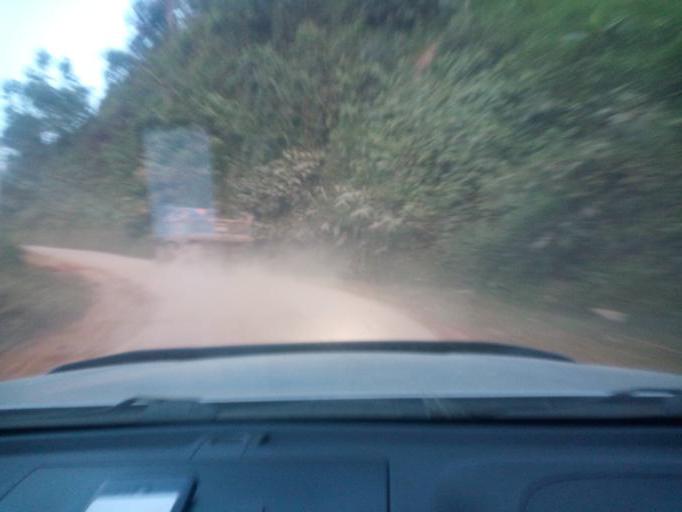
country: VN
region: Yen Bai
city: Co Phuc
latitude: 21.8534
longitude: 104.6158
